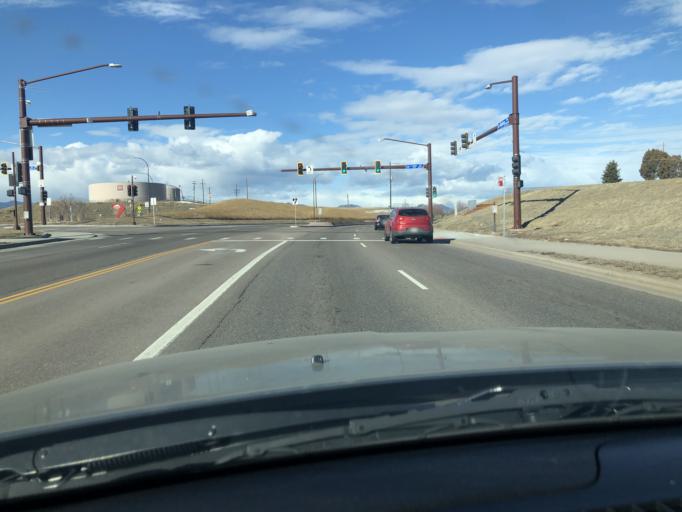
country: US
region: Colorado
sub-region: Jefferson County
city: Arvada
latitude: 39.7957
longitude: -105.1113
